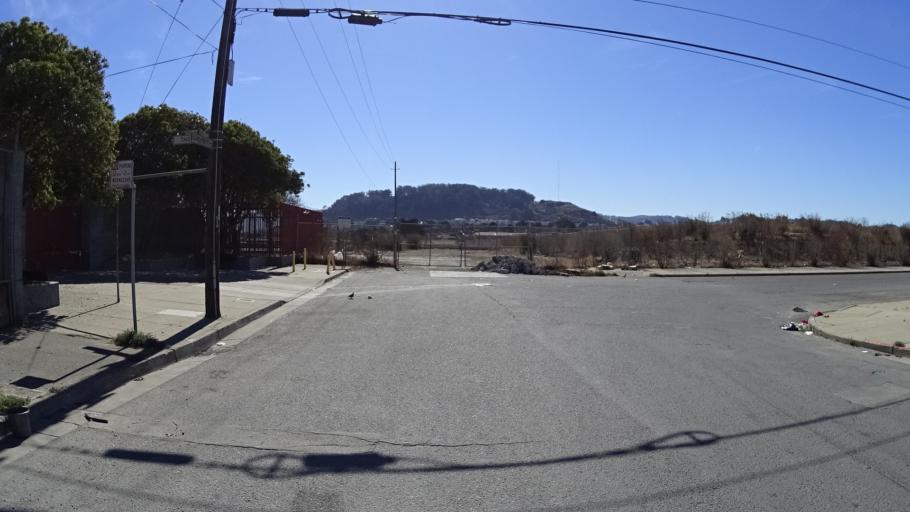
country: US
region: California
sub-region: San Mateo County
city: Brisbane
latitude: 37.7253
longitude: -122.3818
